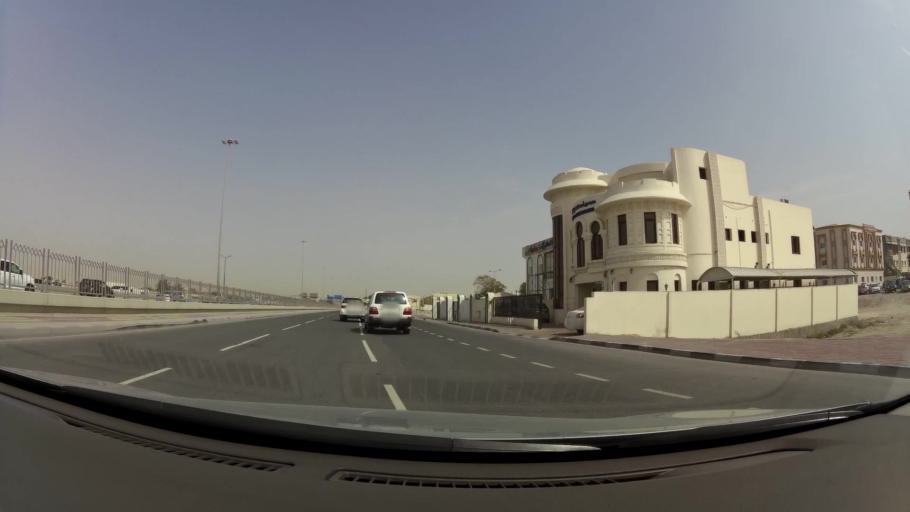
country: QA
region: Baladiyat ar Rayyan
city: Ar Rayyan
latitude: 25.3061
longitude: 51.4732
